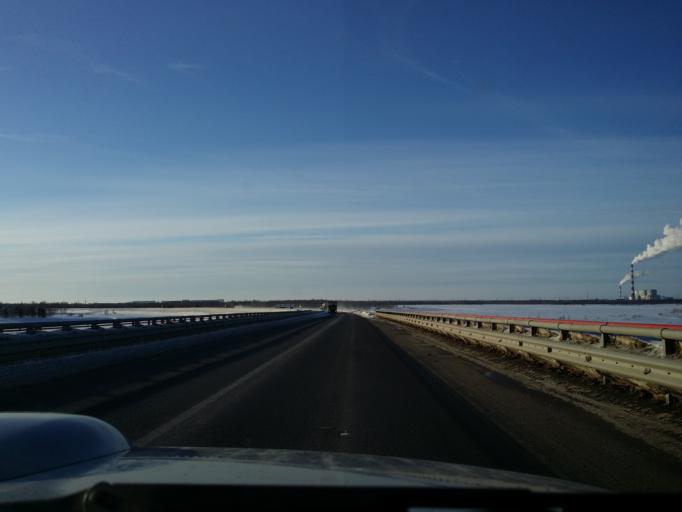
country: RU
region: Khanty-Mansiyskiy Avtonomnyy Okrug
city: Izluchinsk
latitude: 60.9342
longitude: 76.9816
